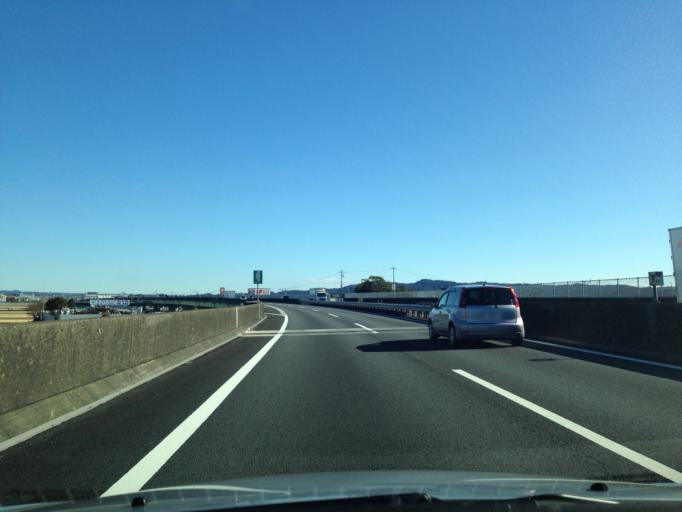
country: JP
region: Shizuoka
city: Fukuroi
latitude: 34.7572
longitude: 137.9317
